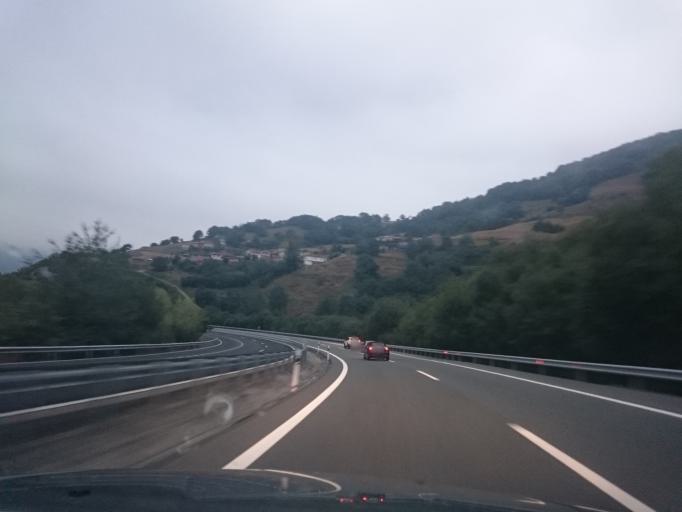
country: ES
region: Asturias
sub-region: Province of Asturias
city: Pola de Lena
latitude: 43.0630
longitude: -5.8208
